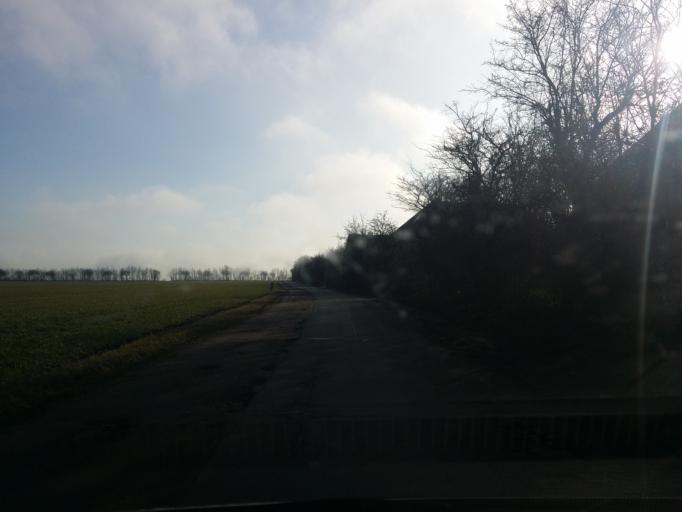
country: DE
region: Schleswig-Holstein
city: Grossenbrode
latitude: 54.4805
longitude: 11.0780
